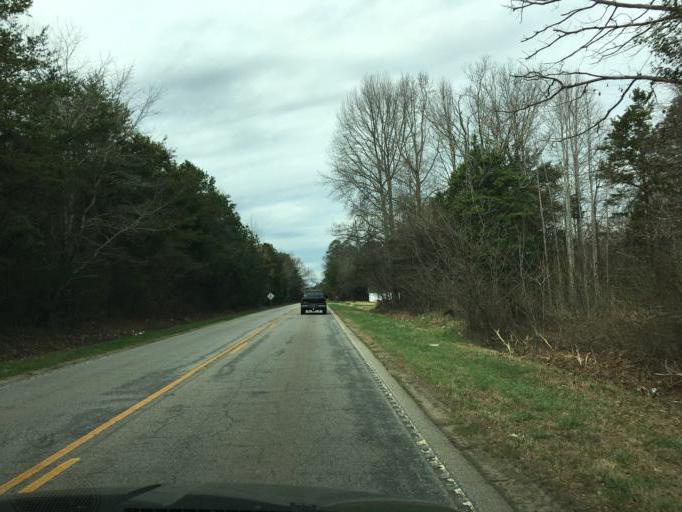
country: US
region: South Carolina
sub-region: Anderson County
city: Piedmont
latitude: 34.7015
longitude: -82.4314
